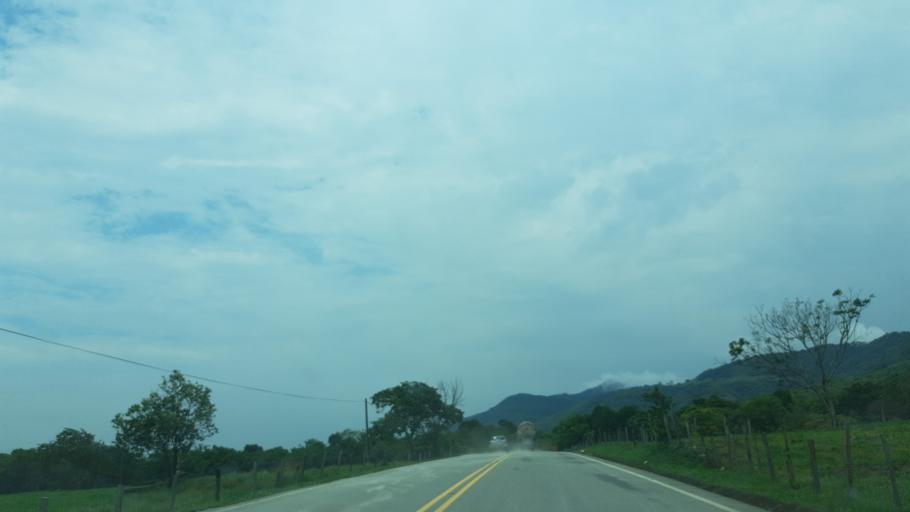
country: CO
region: Casanare
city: Sabanalarga
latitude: 4.7798
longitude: -72.9999
